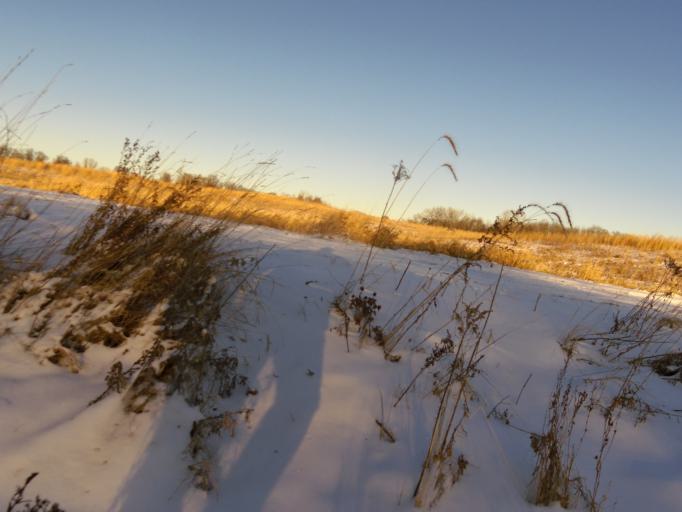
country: US
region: Minnesota
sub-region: Washington County
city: Lake Elmo
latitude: 44.9821
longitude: -92.9033
